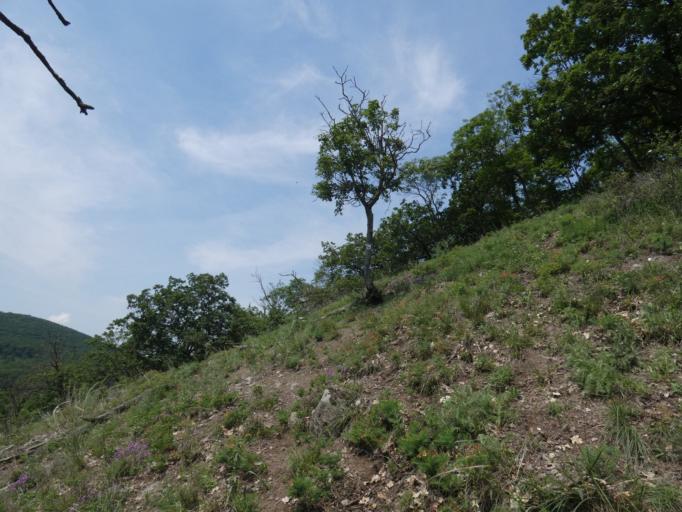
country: HU
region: Pest
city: Szob
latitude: 47.8595
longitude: 18.8479
